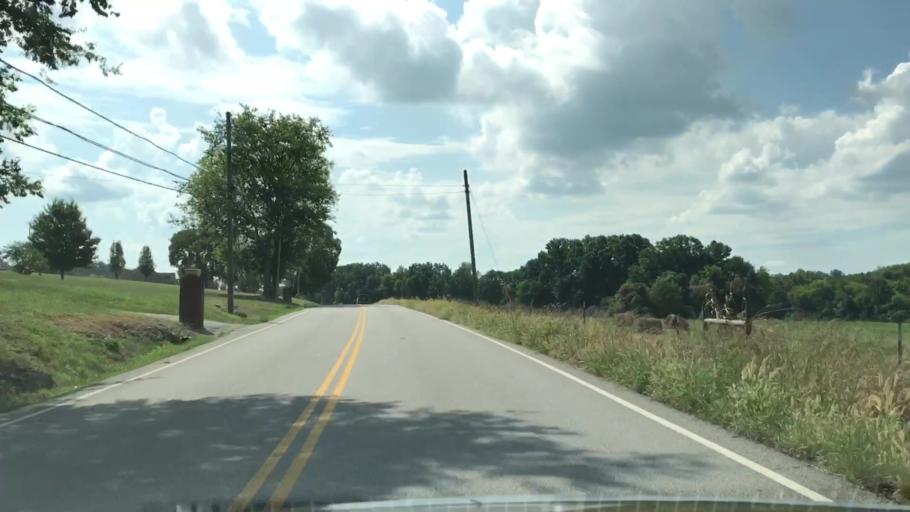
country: US
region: Tennessee
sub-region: Trousdale County
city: Hartsville
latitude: 36.4134
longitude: -86.1790
